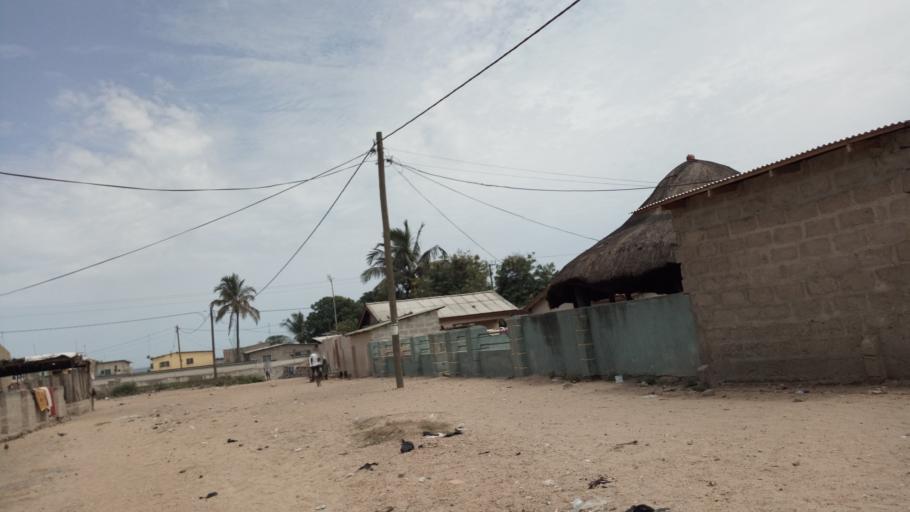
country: GH
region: Central
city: Winneba
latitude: 5.3490
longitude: -0.6145
